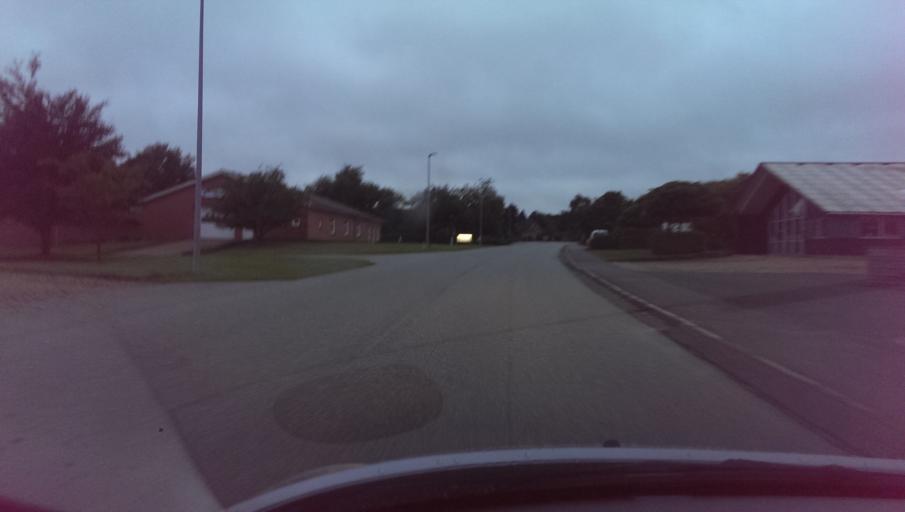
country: DK
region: South Denmark
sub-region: Varde Kommune
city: Olgod
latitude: 55.8145
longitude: 8.6293
